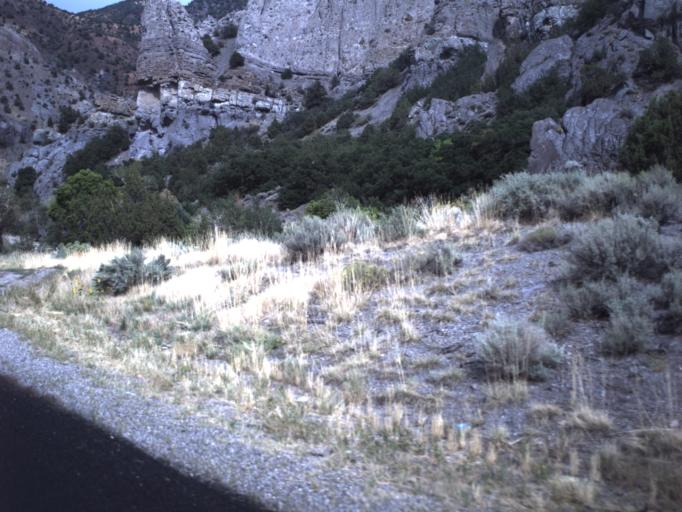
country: US
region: Utah
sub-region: Sevier County
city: Monroe
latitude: 38.5343
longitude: -112.2702
